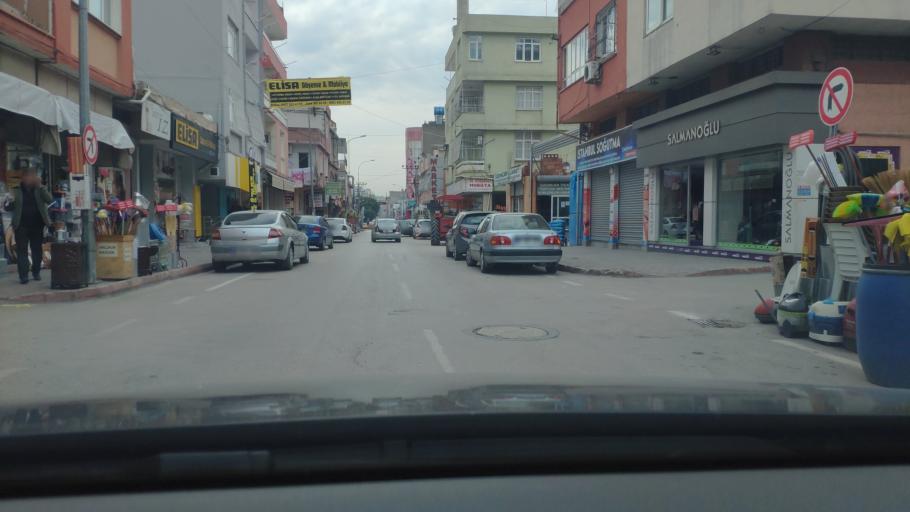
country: TR
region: Adana
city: Adana
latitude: 37.0158
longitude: 35.3144
